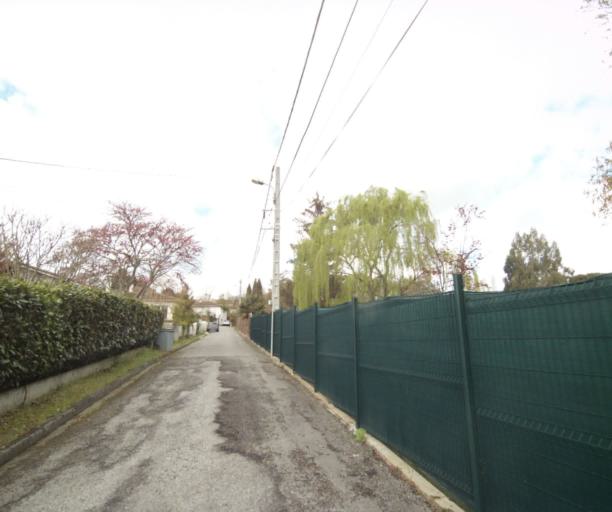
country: FR
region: Midi-Pyrenees
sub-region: Departement de l'Ariege
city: Saverdun
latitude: 43.2291
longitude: 1.5722
